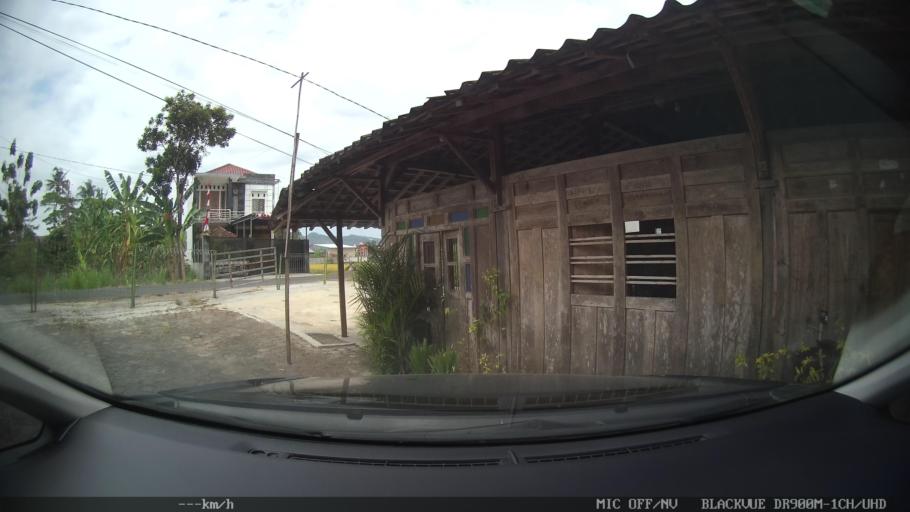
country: ID
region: Central Java
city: Candi Prambanan
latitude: -7.7878
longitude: 110.4810
